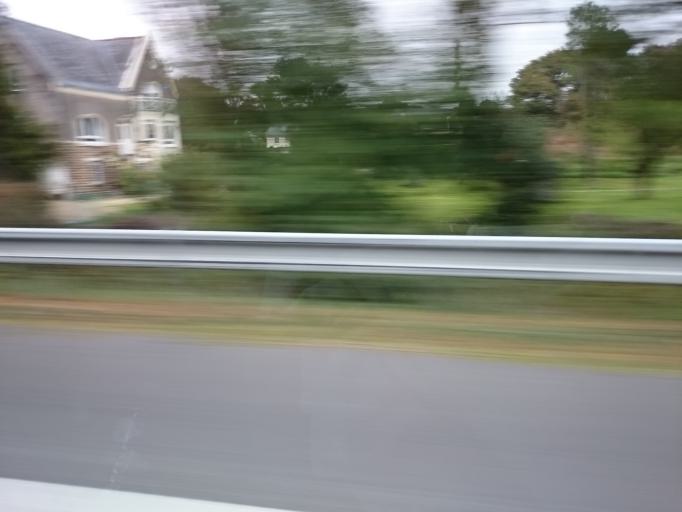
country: FR
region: Brittany
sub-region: Departement du Morbihan
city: Landevant
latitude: 47.7509
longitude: -3.1077
